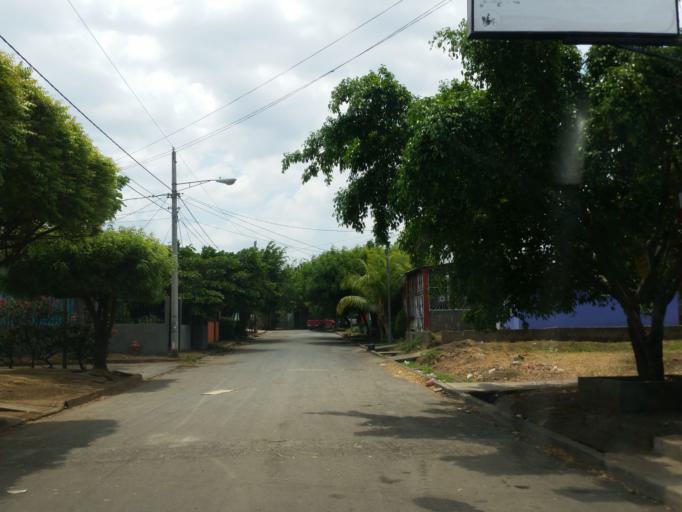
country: NI
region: Managua
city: Managua
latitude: 12.1269
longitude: -86.1893
